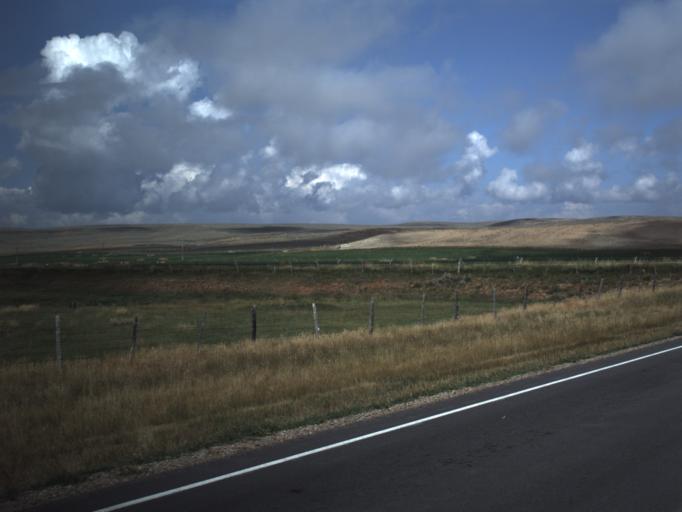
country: US
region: Utah
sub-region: Rich County
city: Randolph
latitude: 41.6745
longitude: -111.1850
